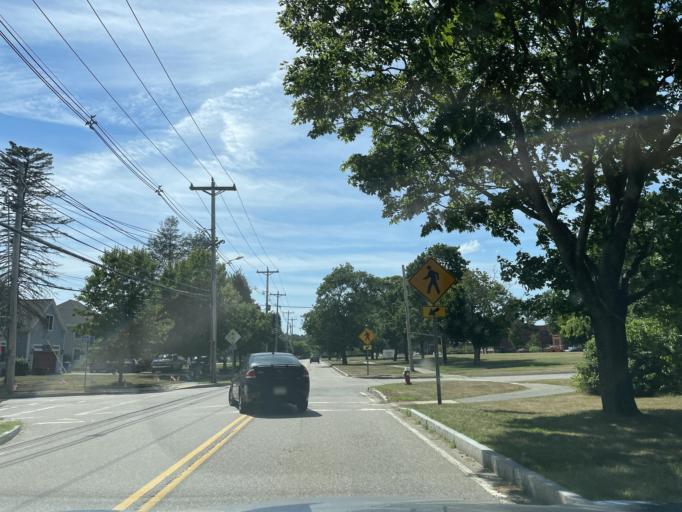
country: US
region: Massachusetts
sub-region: Norfolk County
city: Foxborough
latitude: 42.0753
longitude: -71.2534
